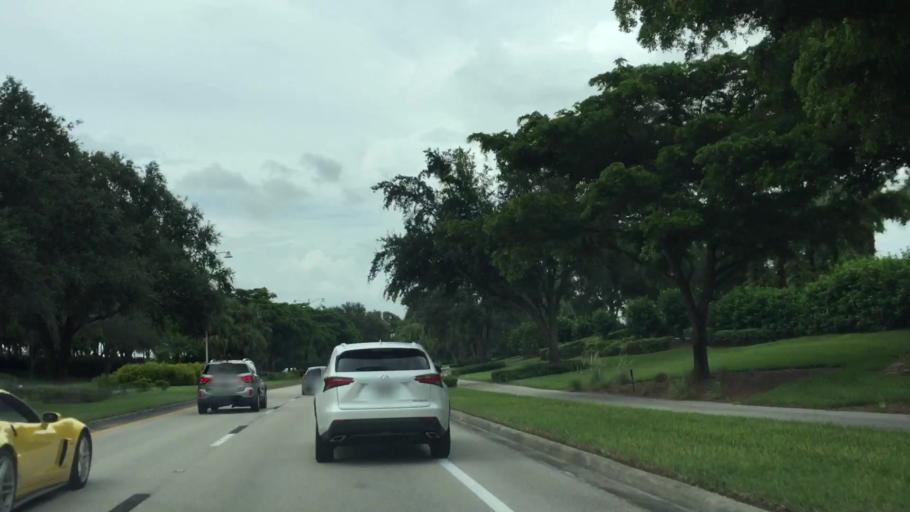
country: US
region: Florida
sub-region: Lee County
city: Estero
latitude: 26.3996
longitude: -81.7844
